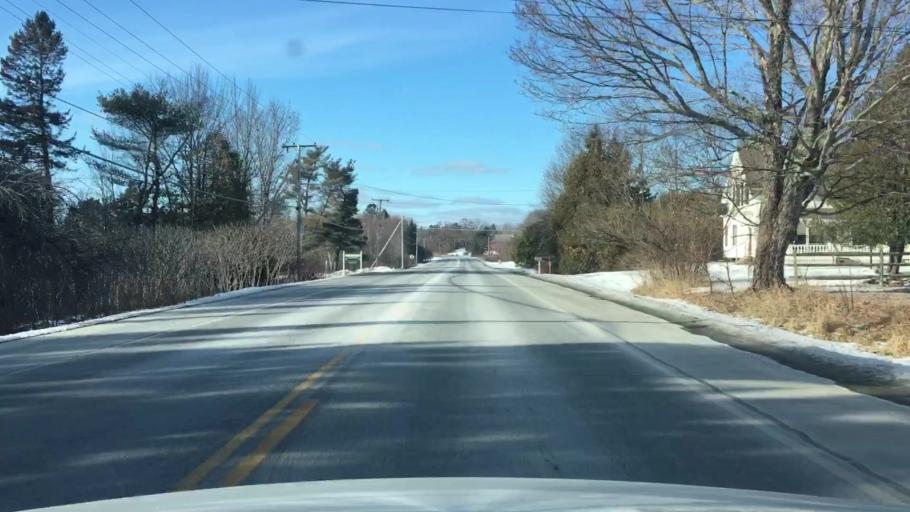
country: US
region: Maine
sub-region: Penobscot County
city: Holden
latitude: 44.7987
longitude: -68.5948
